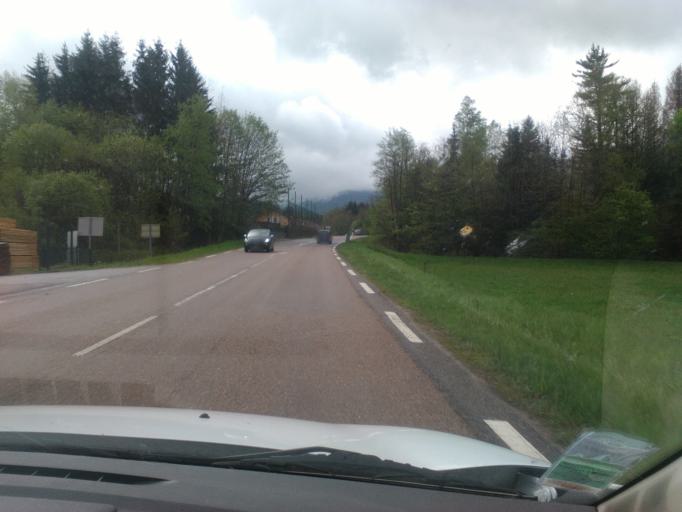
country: FR
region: Lorraine
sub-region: Departement des Vosges
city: Vagney
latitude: 47.9879
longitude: 6.7210
